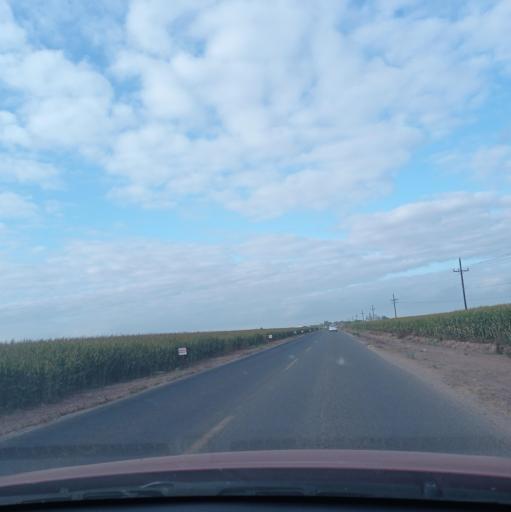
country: MX
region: Sinaloa
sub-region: Guasave
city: Las Quemazones
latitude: 25.6643
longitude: -108.5193
